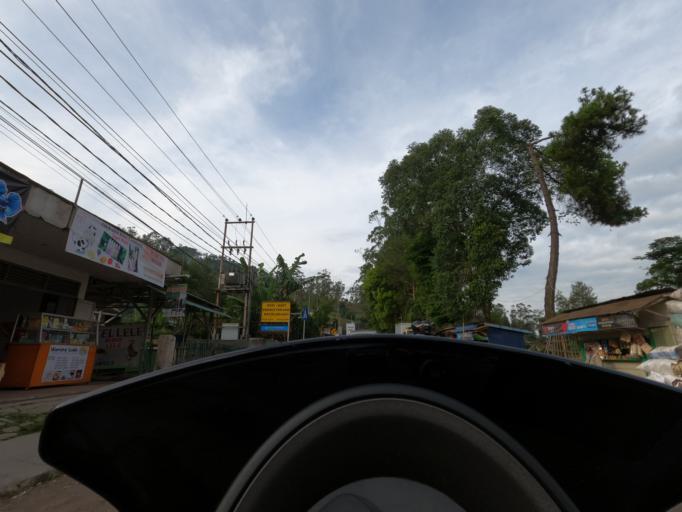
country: ID
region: West Java
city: Lembang
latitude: -6.8101
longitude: 107.6356
